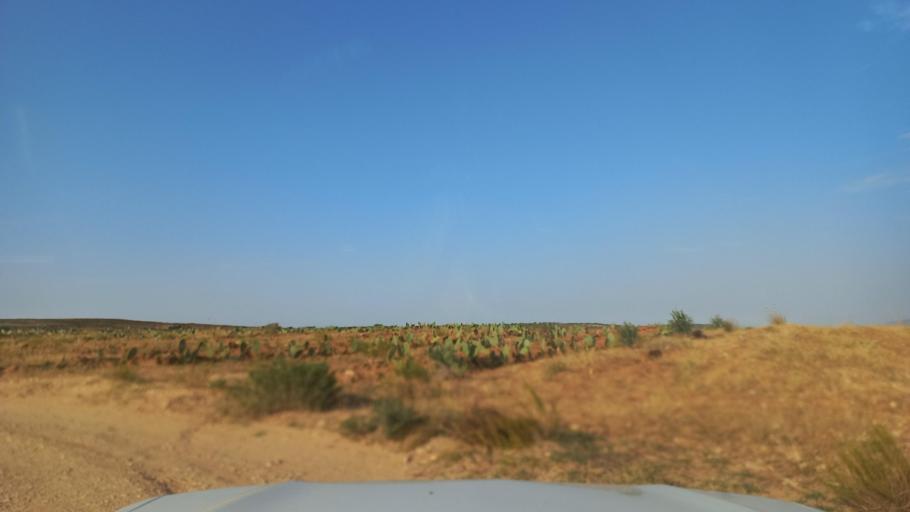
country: TN
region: Al Qasrayn
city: Kasserine
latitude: 35.3576
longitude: 8.8417
